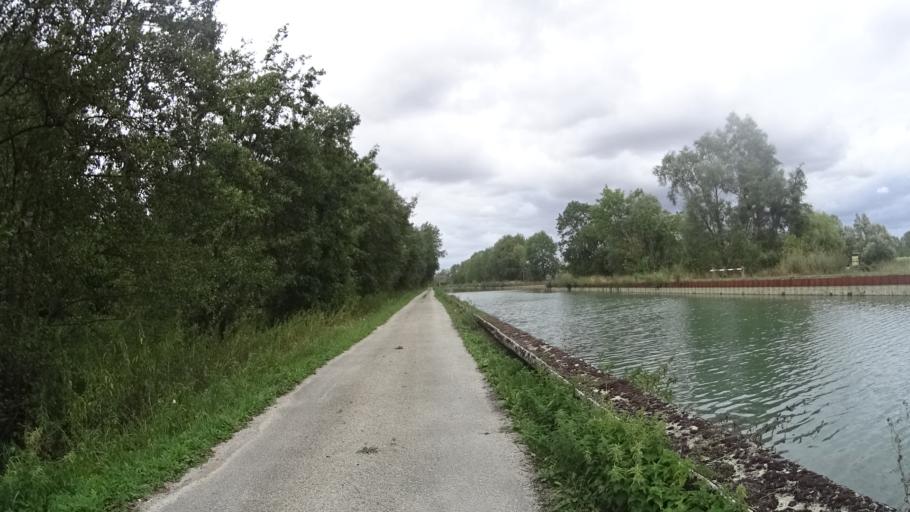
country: FR
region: Picardie
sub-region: Departement de l'Aisne
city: La Fere
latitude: 49.6912
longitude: 3.3682
